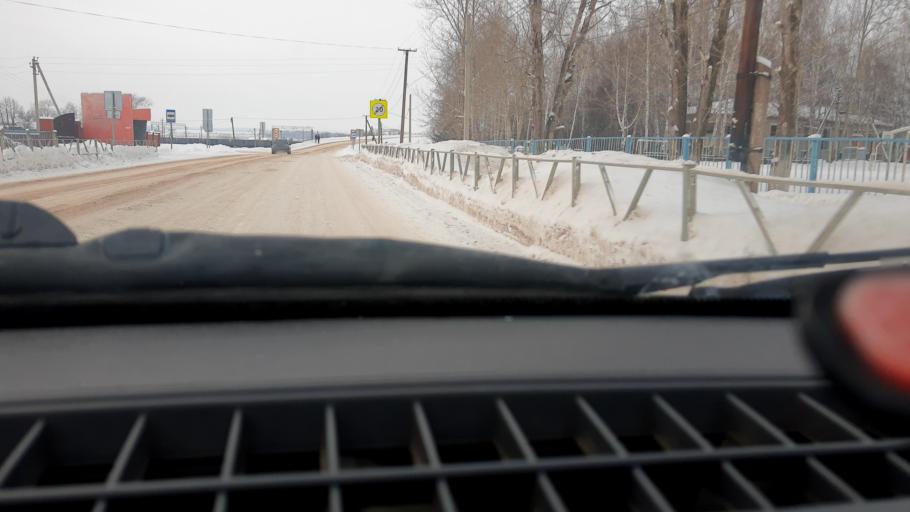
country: RU
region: Bashkortostan
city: Davlekanovo
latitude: 54.5801
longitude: 54.9348
